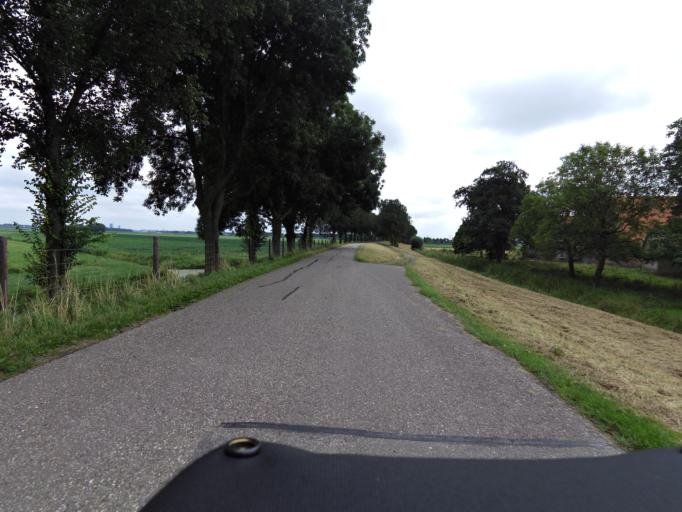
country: NL
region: South Holland
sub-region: Gemeente Maassluis
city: Maassluis
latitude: 51.8539
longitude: 4.2533
